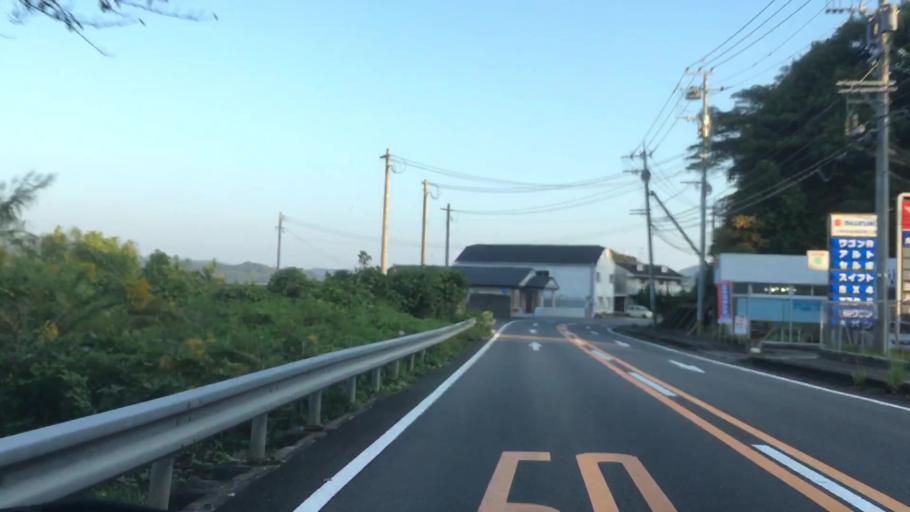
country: JP
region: Nagasaki
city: Sasebo
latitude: 33.0143
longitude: 129.7337
